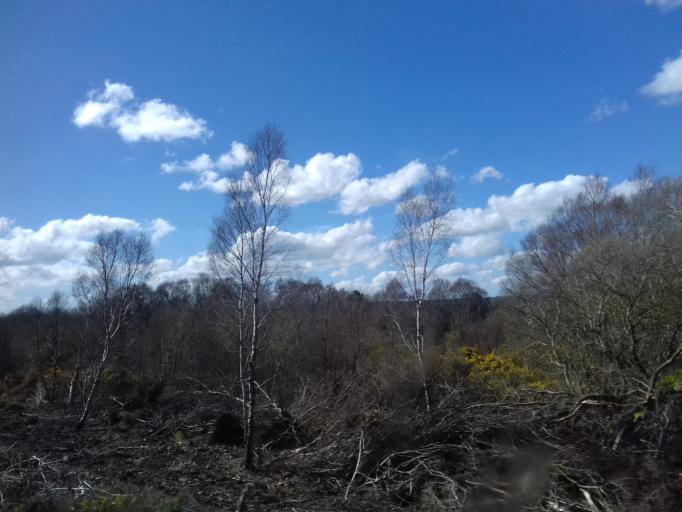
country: IE
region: Munster
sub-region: County Cork
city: Millstreet
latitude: 52.0881
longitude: -8.9994
